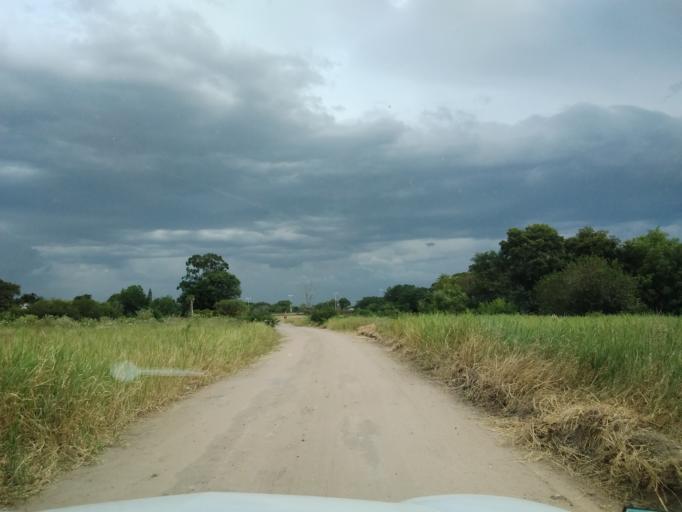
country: AR
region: Corrientes
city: Corrientes
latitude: -27.5218
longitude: -58.7964
